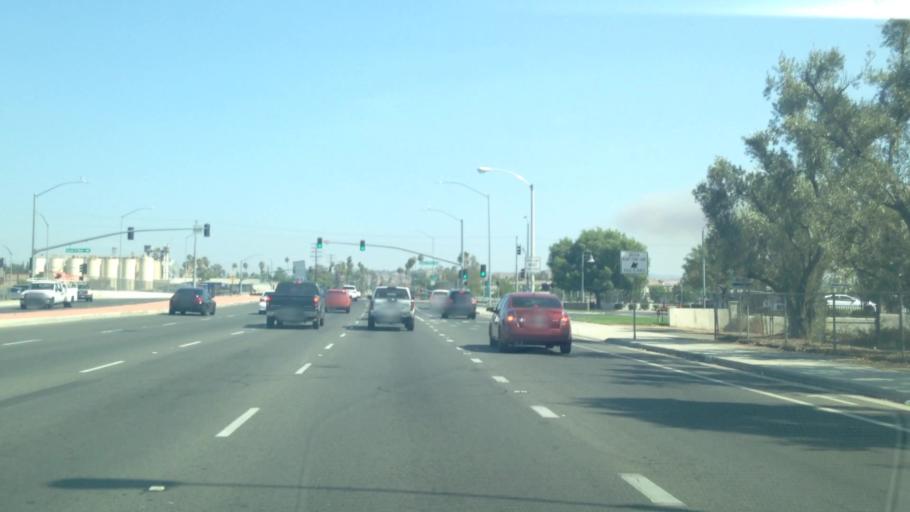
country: US
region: California
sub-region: Riverside County
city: Riverside
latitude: 33.9156
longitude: -117.4432
